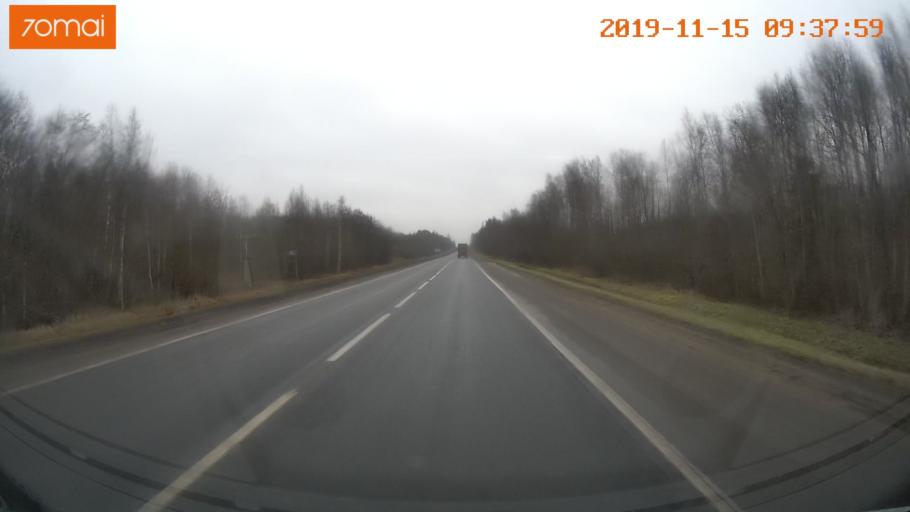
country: RU
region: Vologda
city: Sheksna
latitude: 59.2361
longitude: 38.4468
